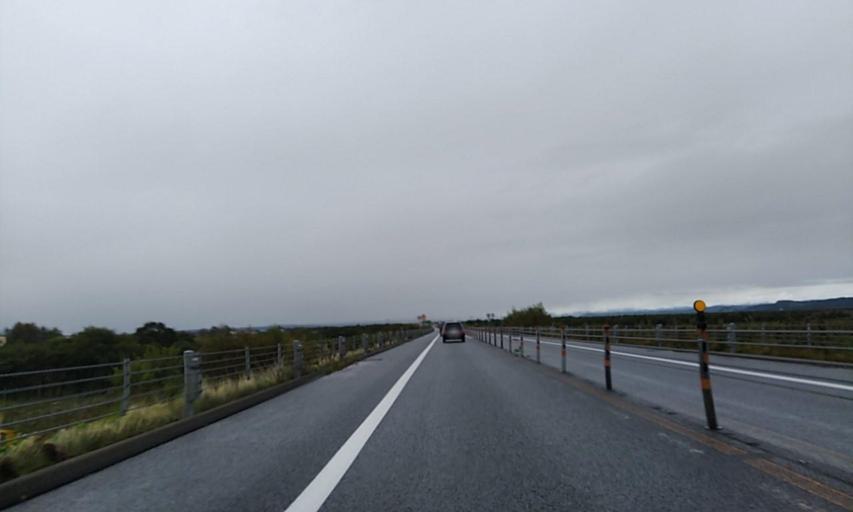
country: JP
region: Hokkaido
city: Kushiro
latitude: 43.0364
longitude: 144.3609
